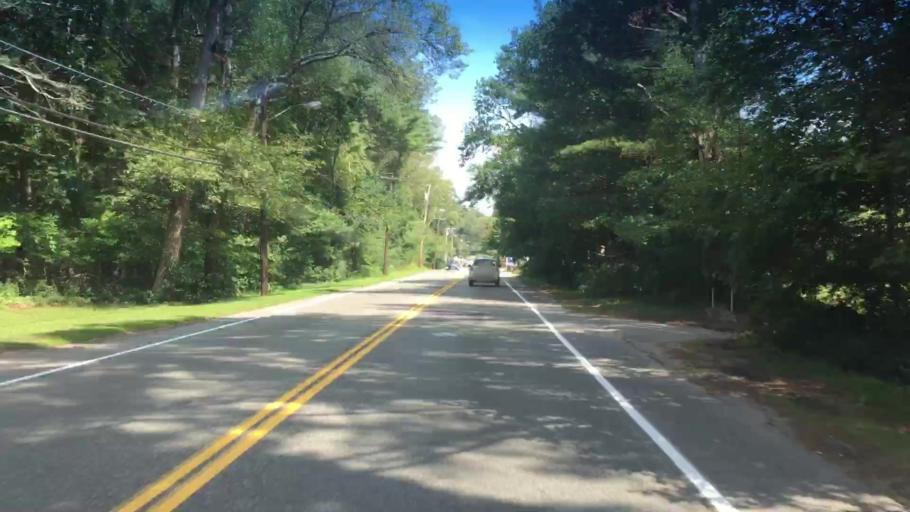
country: US
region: Massachusetts
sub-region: Norfolk County
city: Medfield
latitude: 42.1880
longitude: -71.3017
